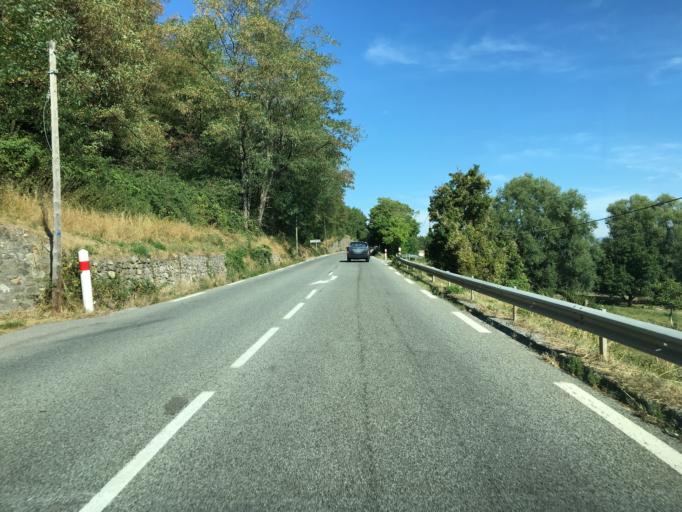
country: FR
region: Provence-Alpes-Cote d'Azur
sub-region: Departement des Alpes-de-Haute-Provence
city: Sisteron
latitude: 44.2470
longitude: 5.8883
